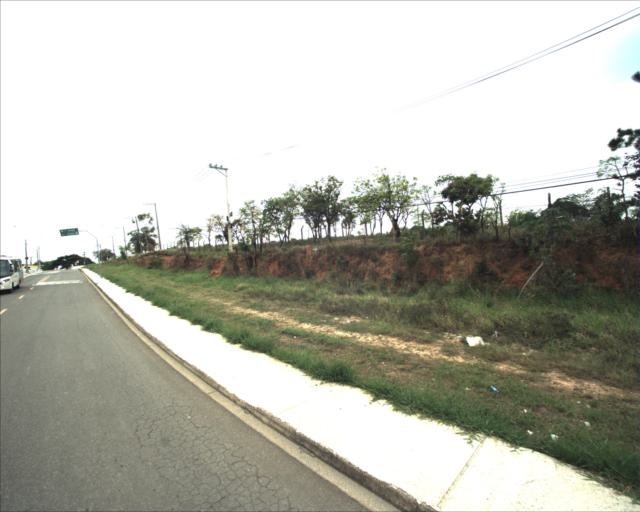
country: BR
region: Sao Paulo
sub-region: Sorocaba
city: Sorocaba
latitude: -23.4495
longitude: -47.3776
